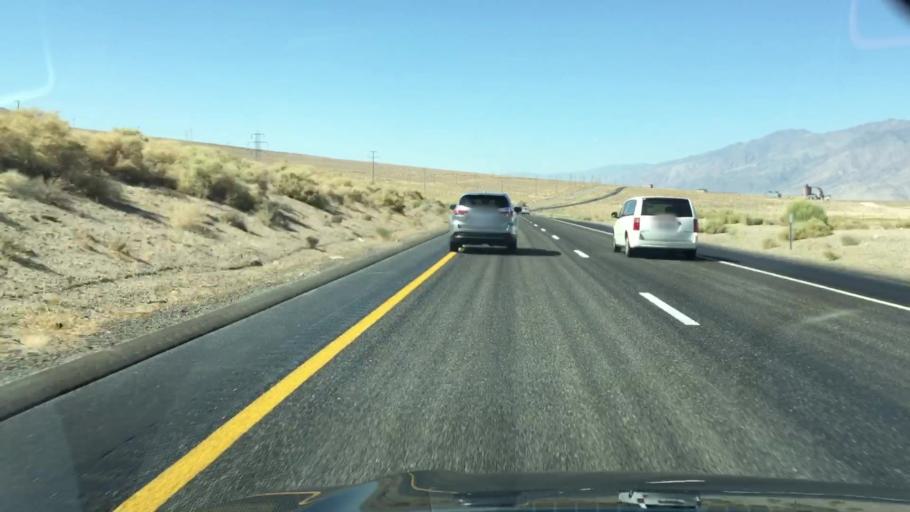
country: US
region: California
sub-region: Inyo County
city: Lone Pine
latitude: 36.4581
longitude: -118.0354
